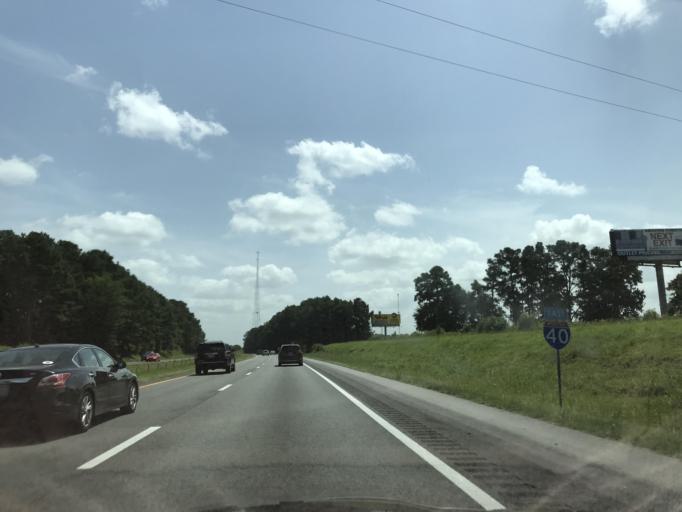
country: US
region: North Carolina
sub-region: Sampson County
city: Plain View
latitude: 35.2428
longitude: -78.3730
